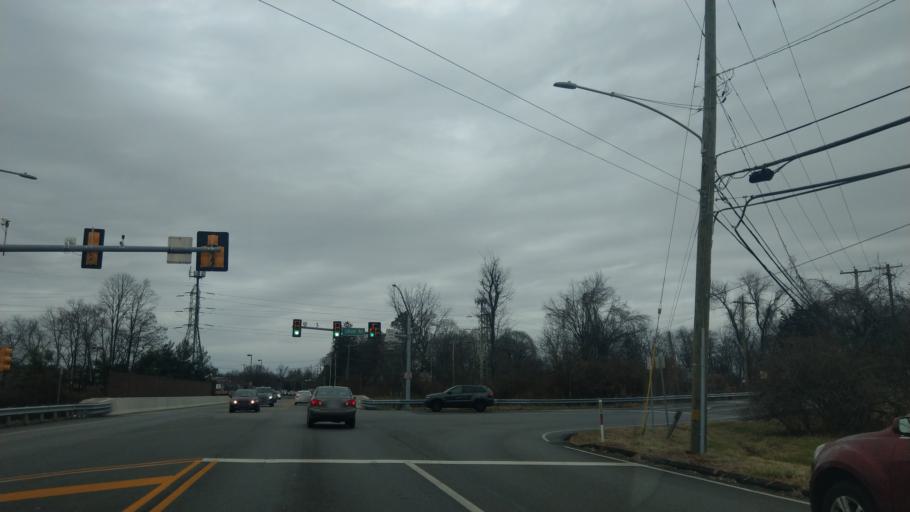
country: US
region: Pennsylvania
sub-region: Bucks County
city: Hulmeville
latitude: 40.1277
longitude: -74.9241
